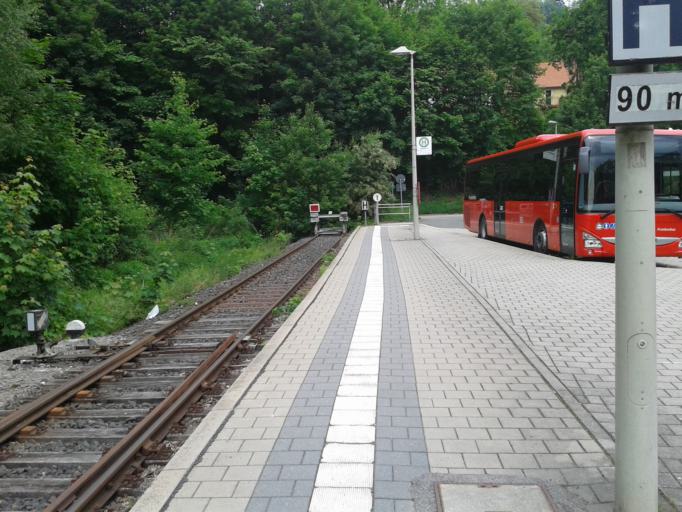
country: DE
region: Bavaria
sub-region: Upper Franconia
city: Grafenberg
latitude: 49.6421
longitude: 11.2503
